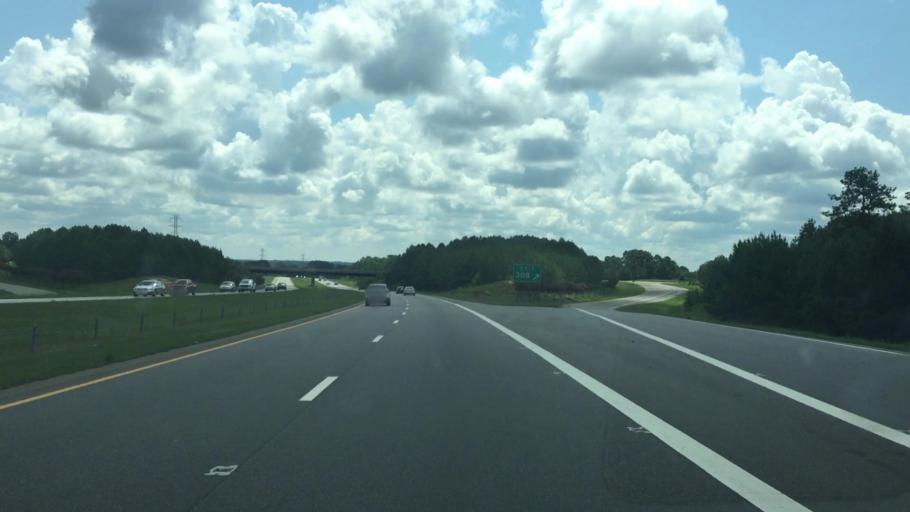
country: US
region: North Carolina
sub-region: Richmond County
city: Cordova
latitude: 34.9333
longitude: -79.8354
